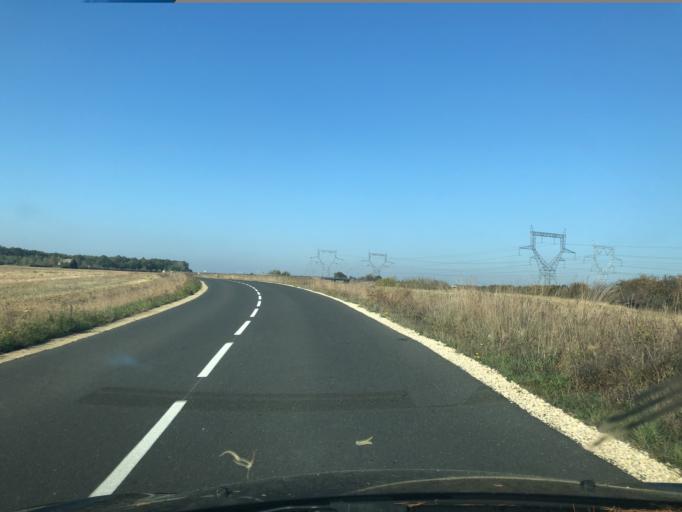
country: FR
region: Centre
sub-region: Departement d'Indre-et-Loire
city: Cerelles
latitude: 47.4919
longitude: 0.6586
